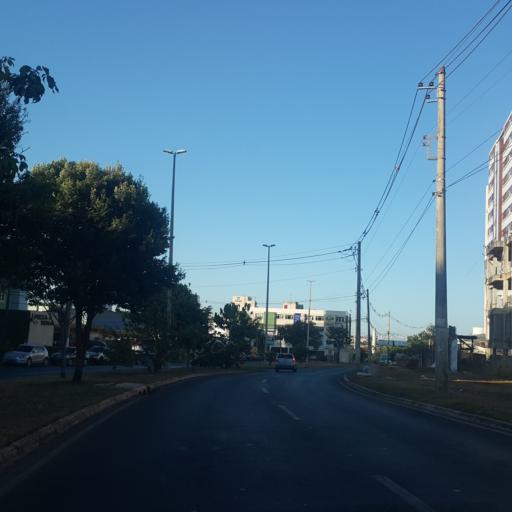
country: BR
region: Federal District
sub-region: Brasilia
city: Brasilia
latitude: -15.8302
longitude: -48.0124
